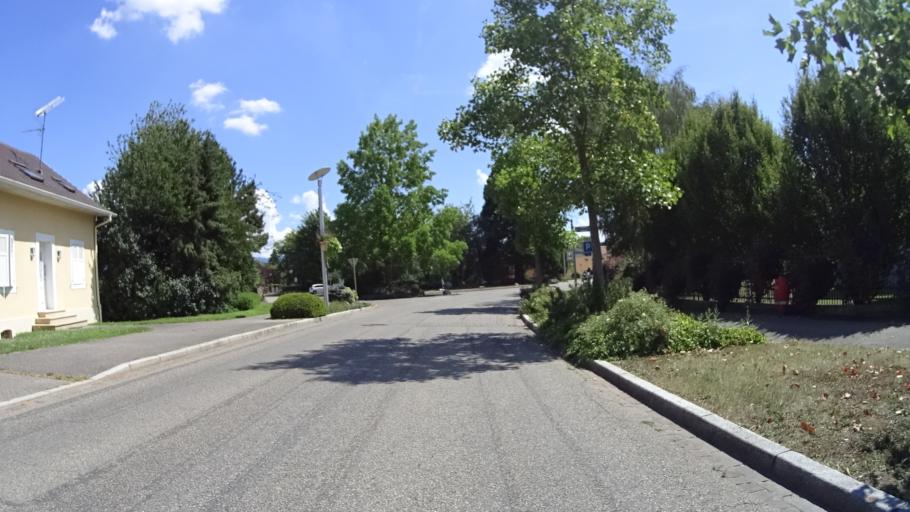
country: FR
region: Alsace
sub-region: Departement du Haut-Rhin
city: Ottmarsheim
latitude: 47.7917
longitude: 7.5049
